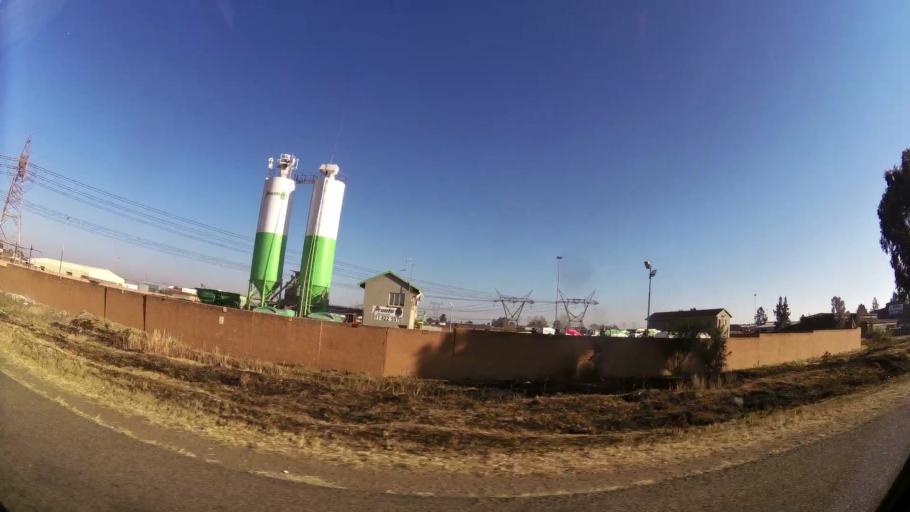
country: ZA
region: Gauteng
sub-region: Ekurhuleni Metropolitan Municipality
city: Germiston
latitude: -26.3563
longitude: 28.1215
